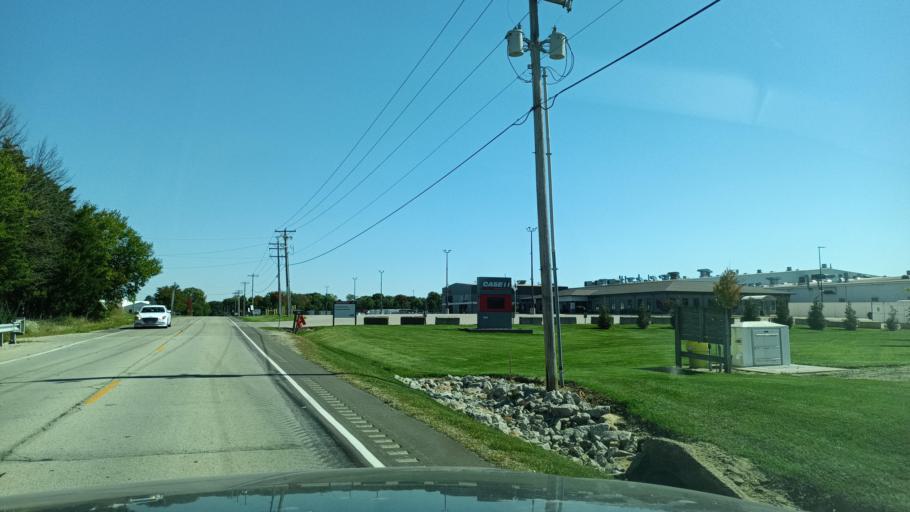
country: US
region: Illinois
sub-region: Woodford County
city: Eureka
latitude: 40.6273
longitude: -89.2644
